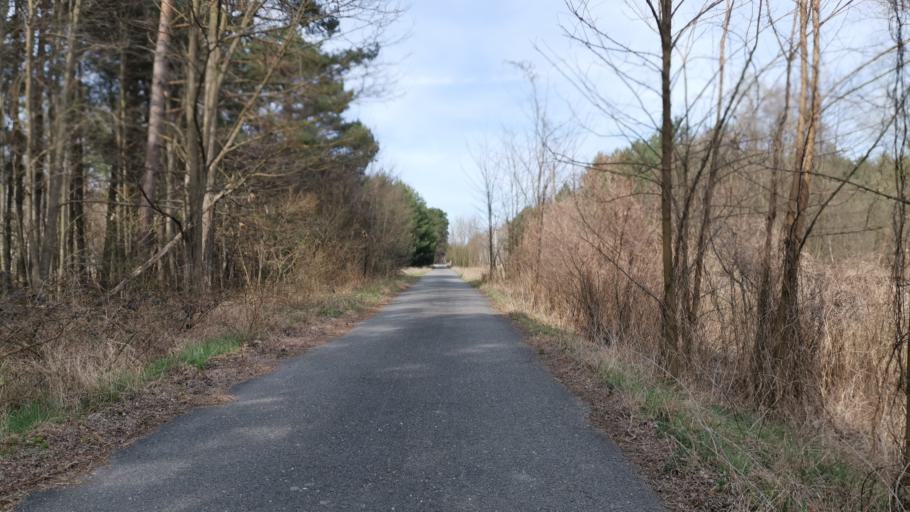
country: SK
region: Trnavsky
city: Gbely
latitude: 48.6775
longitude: 17.0584
